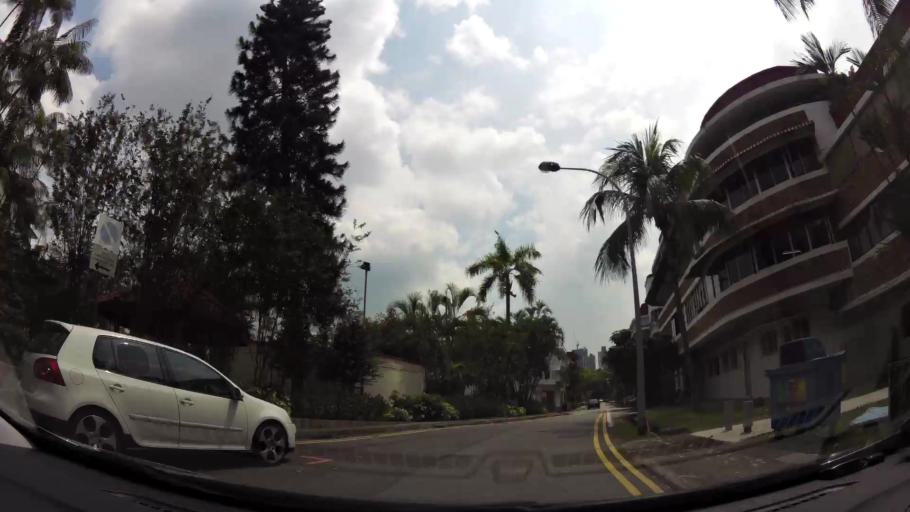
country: SG
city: Singapore
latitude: 1.2838
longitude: 103.8309
